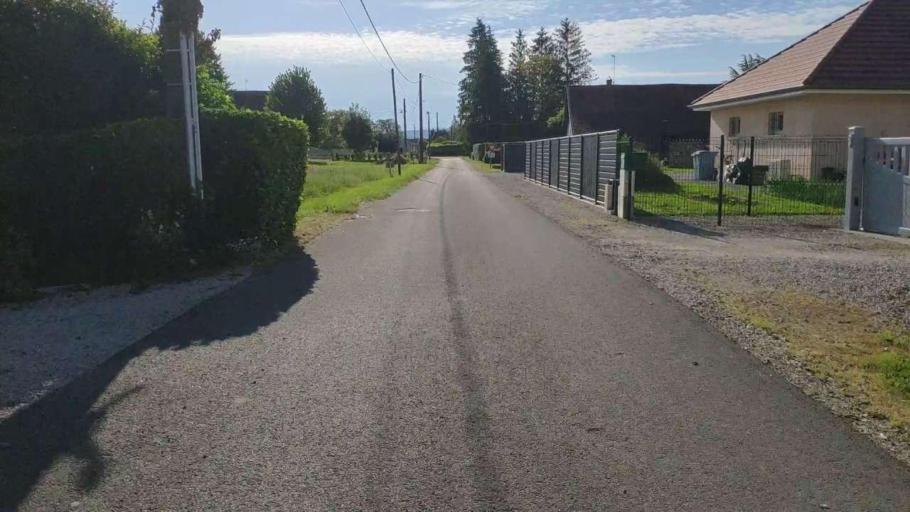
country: FR
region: Franche-Comte
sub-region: Departement du Jura
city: Bletterans
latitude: 46.7405
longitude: 5.4590
